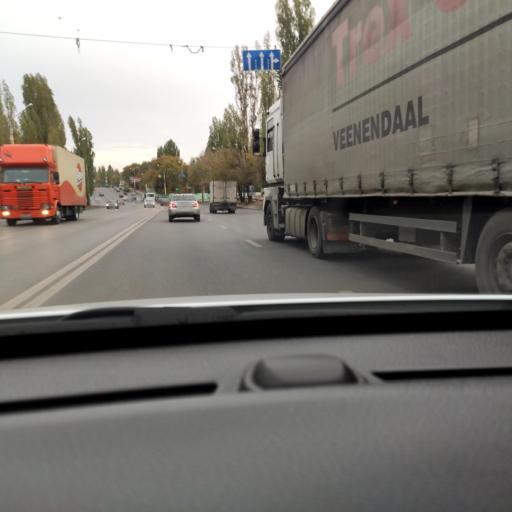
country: RU
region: Voronezj
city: Voronezh
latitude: 51.6253
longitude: 39.2322
